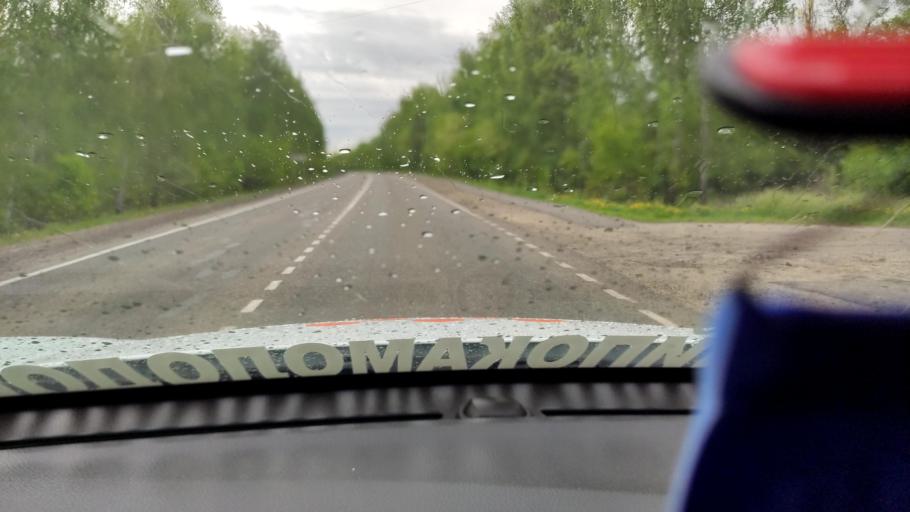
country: RU
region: Voronezj
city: Imeni Pervogo Maya
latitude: 50.7488
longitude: 39.3873
